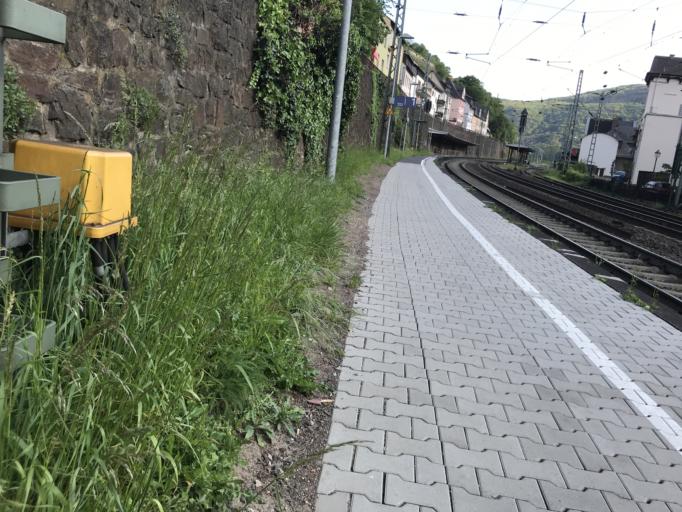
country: DE
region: Rheinland-Pfalz
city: Weiler
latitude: 49.9866
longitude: 7.8672
